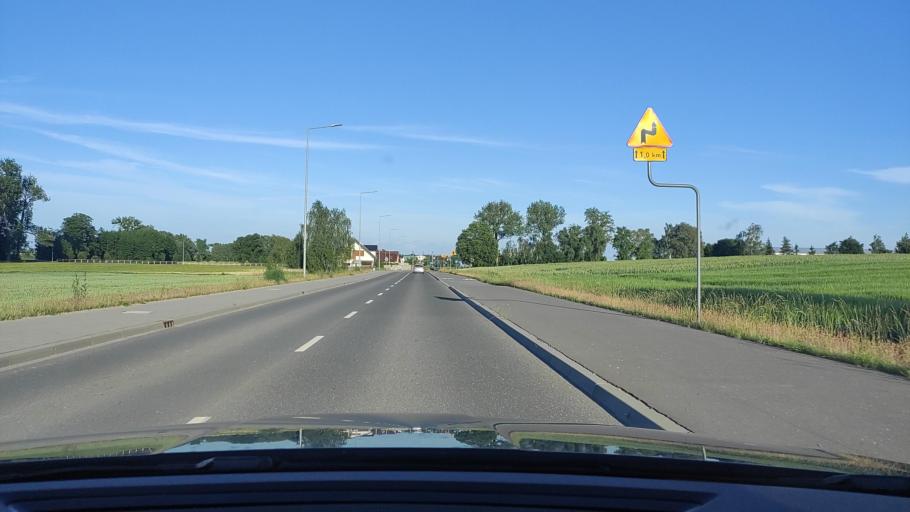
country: PL
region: Greater Poland Voivodeship
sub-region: Powiat poznanski
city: Kornik
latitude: 52.3086
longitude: 17.0715
